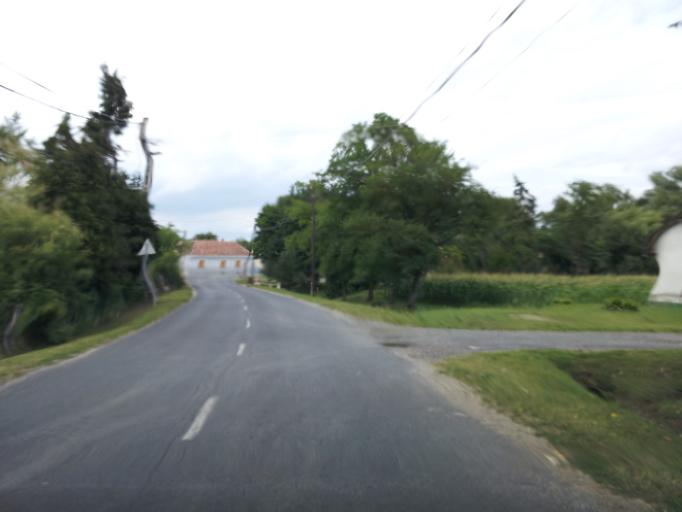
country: HU
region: Zala
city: Zalaszentgrot
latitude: 47.0309
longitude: 16.9743
